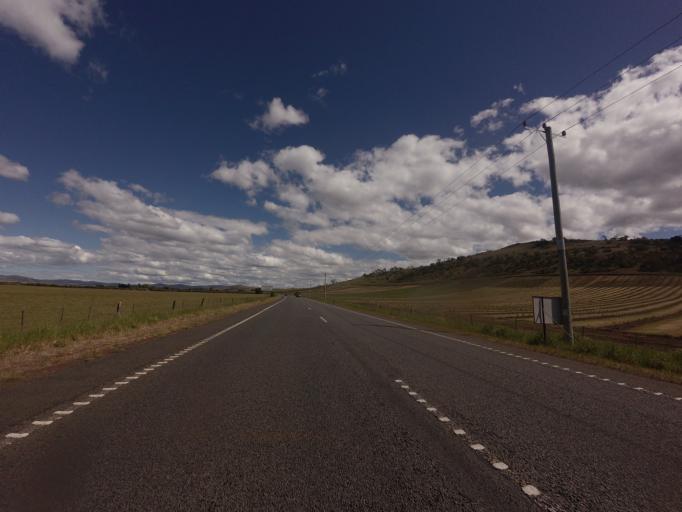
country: AU
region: Tasmania
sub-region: Northern Midlands
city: Evandale
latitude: -42.0468
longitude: 147.4821
